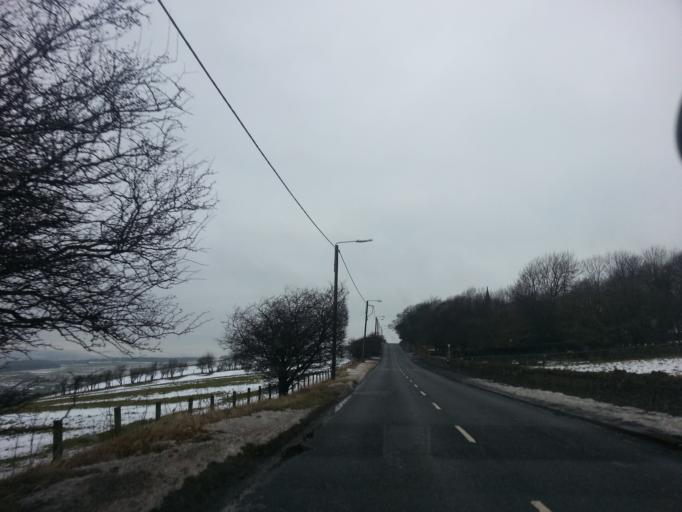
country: GB
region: England
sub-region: County Durham
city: Crook
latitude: 54.7359
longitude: -1.7522
